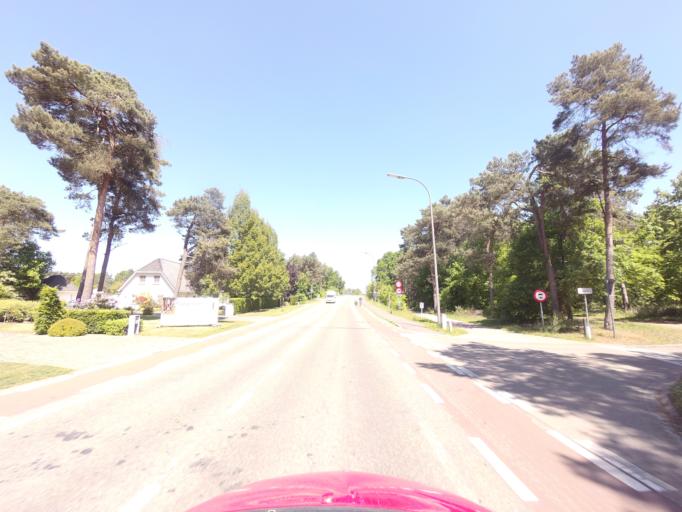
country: BE
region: Flanders
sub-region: Provincie Limburg
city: Lommel
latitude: 51.2512
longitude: 5.3111
